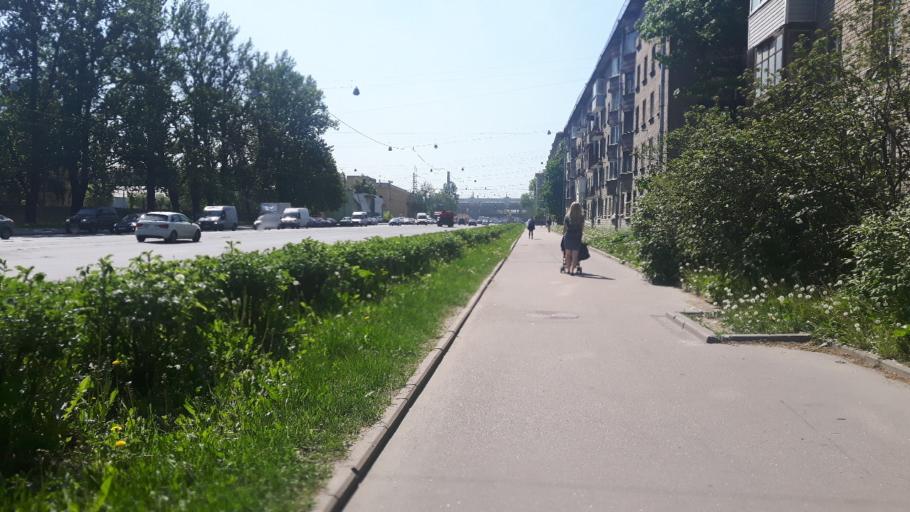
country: RU
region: St.-Petersburg
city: Avtovo
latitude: 59.8878
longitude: 30.2758
